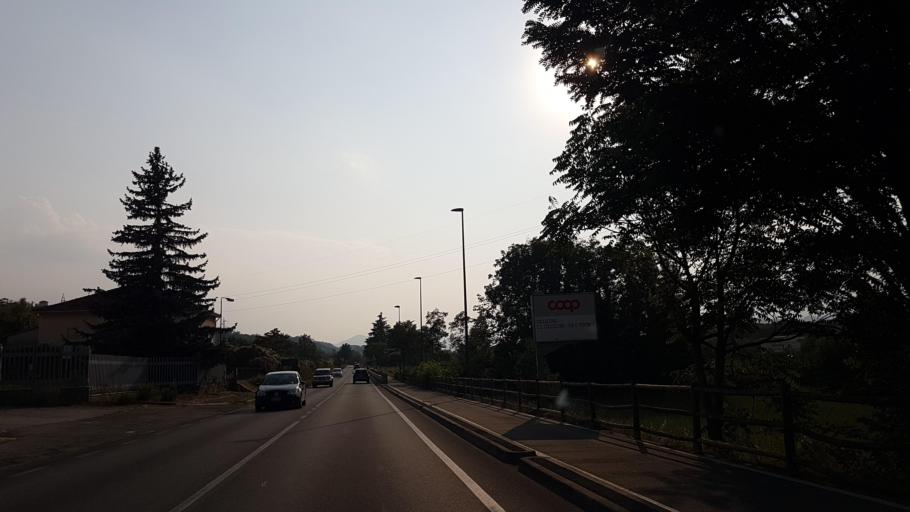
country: IT
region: Emilia-Romagna
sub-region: Provincia di Parma
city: Ozzano Taro
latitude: 44.7082
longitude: 10.1376
